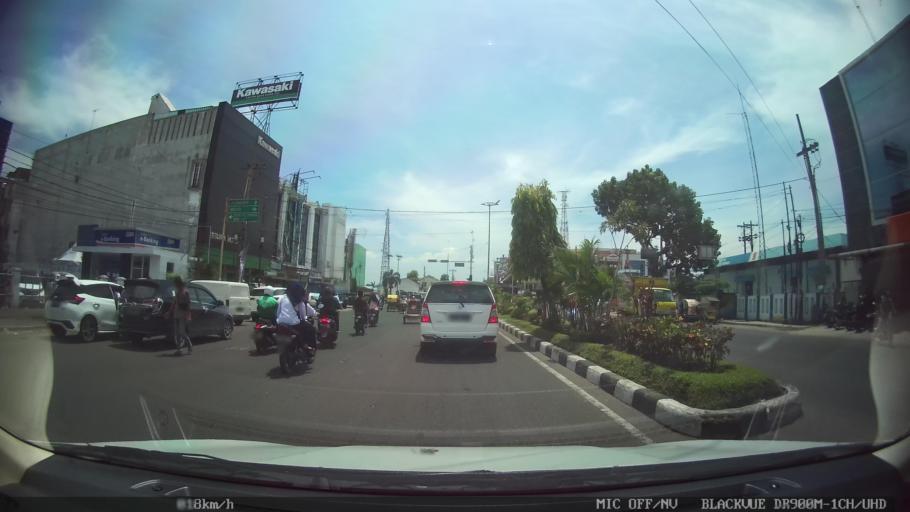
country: ID
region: North Sumatra
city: Binjai
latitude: 3.6105
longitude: 98.4936
